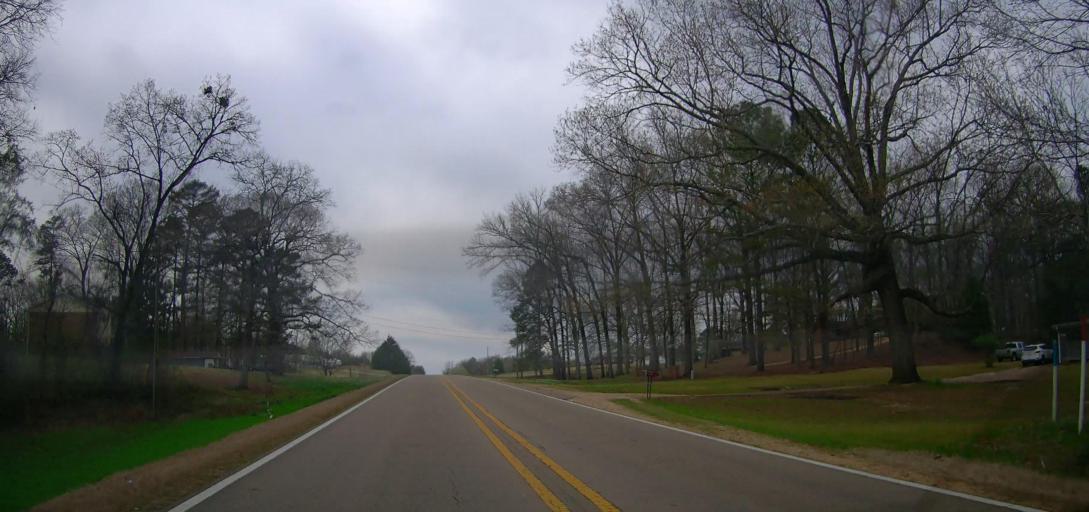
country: US
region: Mississippi
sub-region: Itawamba County
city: Mantachie
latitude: 34.2583
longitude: -88.5084
